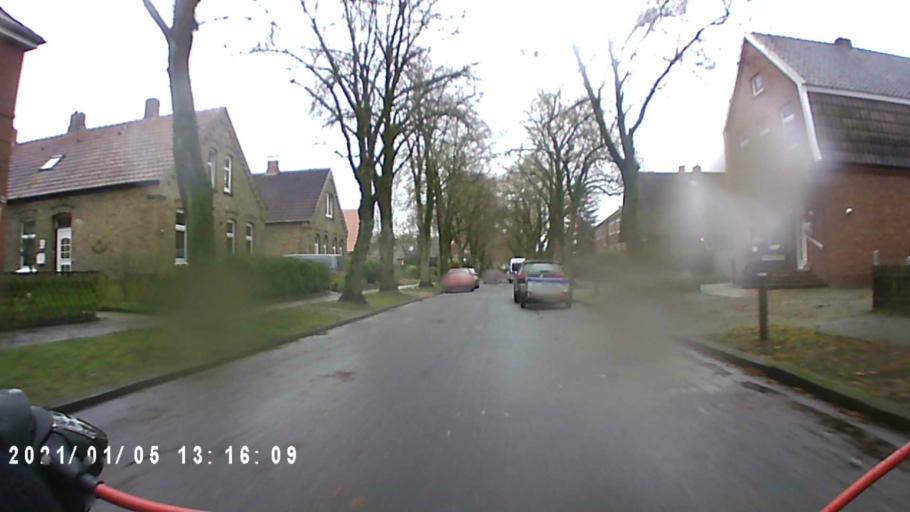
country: DE
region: Lower Saxony
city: Leer
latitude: 53.2376
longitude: 7.4511
